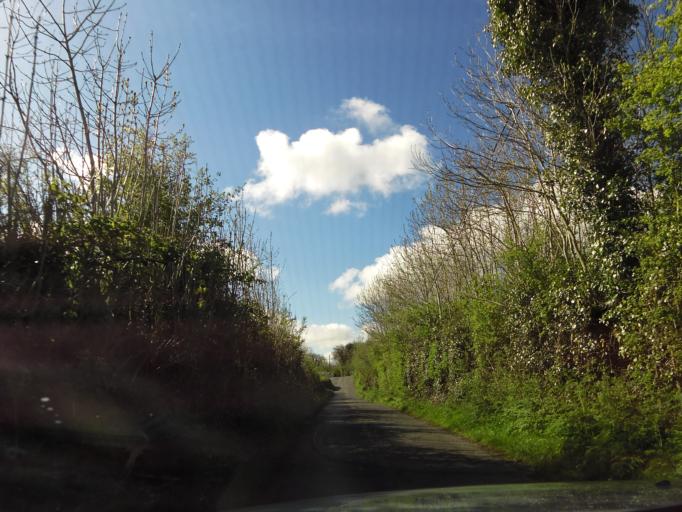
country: IE
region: Connaught
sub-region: Maigh Eo
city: Kiltamagh
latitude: 53.7876
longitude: -8.9626
